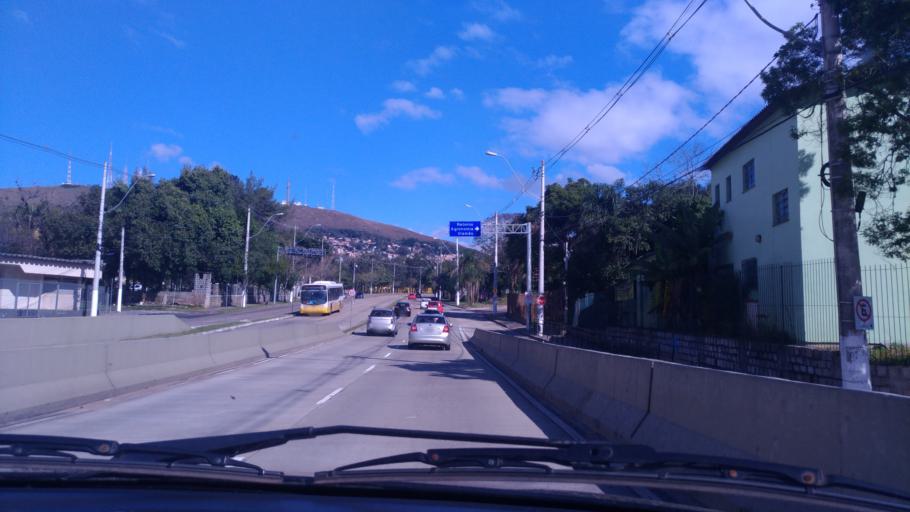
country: BR
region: Rio Grande do Sul
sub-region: Porto Alegre
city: Porto Alegre
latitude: -30.0650
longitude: -51.1865
